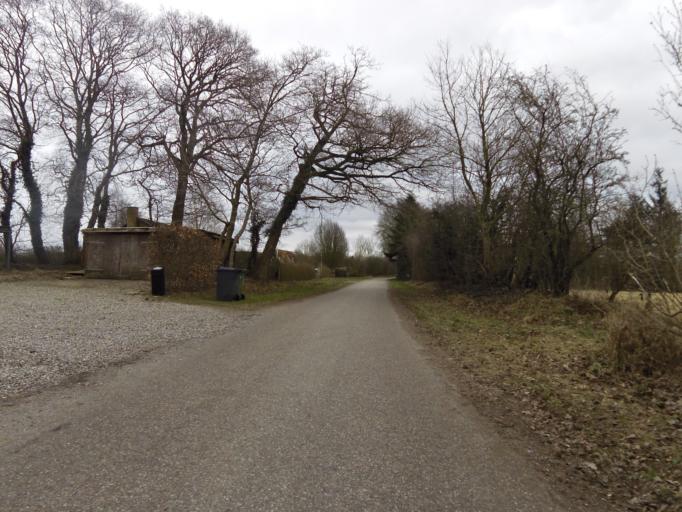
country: DK
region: South Denmark
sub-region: Tonder Kommune
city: Toftlund
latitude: 55.2082
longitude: 9.1792
